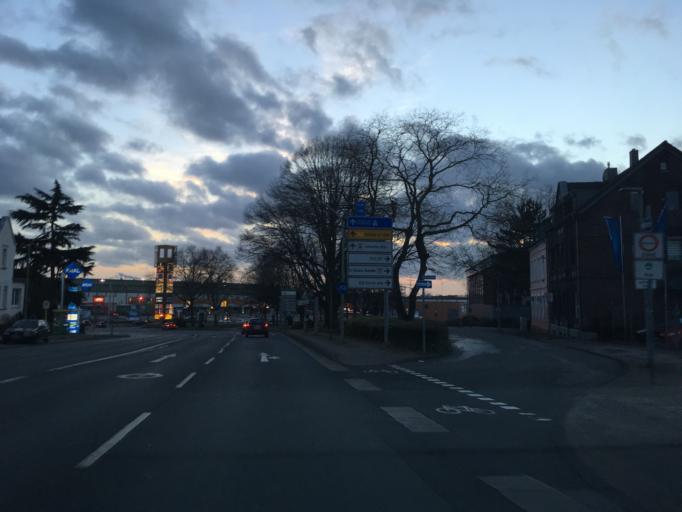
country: DE
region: North Rhine-Westphalia
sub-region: Regierungsbezirk Dusseldorf
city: Oberhausen
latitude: 51.5179
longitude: 6.8573
